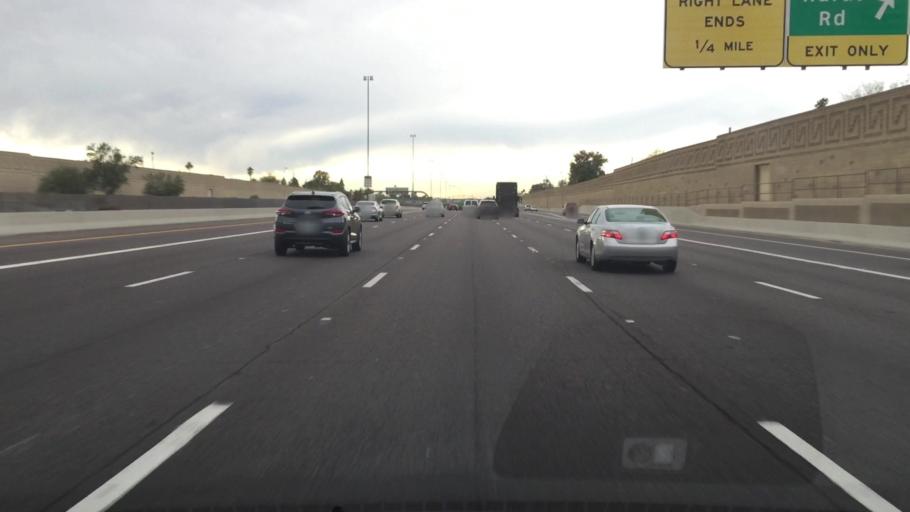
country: US
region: Arizona
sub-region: Maricopa County
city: Tempe
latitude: 33.3835
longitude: -111.9167
